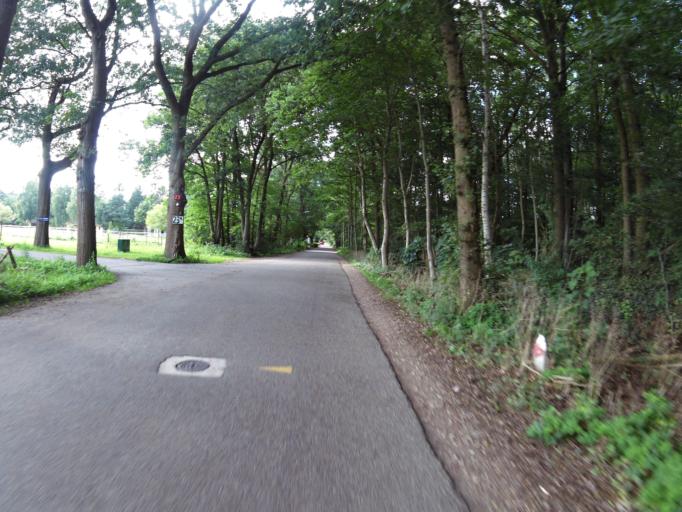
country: NL
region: North Holland
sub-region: Gemeente Wijdemeren
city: Nieuw-Loosdrecht
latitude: 52.1787
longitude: 5.1710
